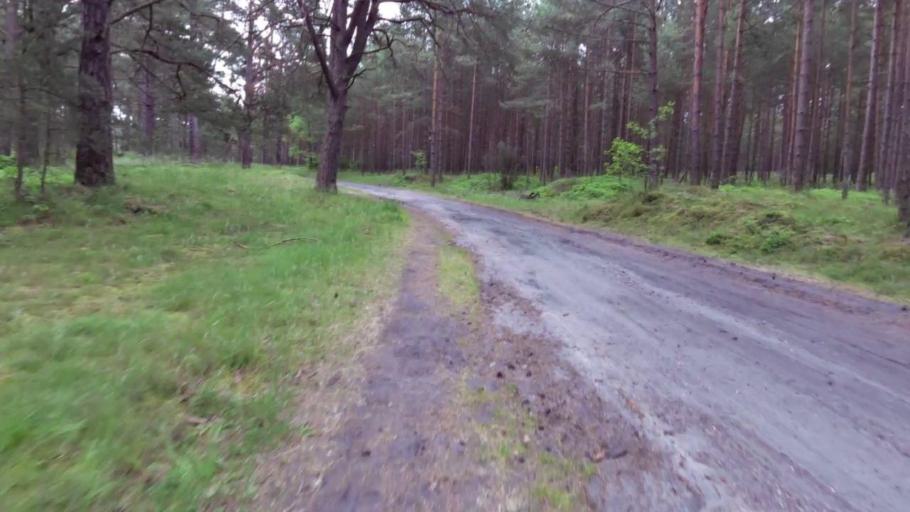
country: PL
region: West Pomeranian Voivodeship
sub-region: Swinoujscie
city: Swinoujscie
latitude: 53.9046
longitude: 14.3310
